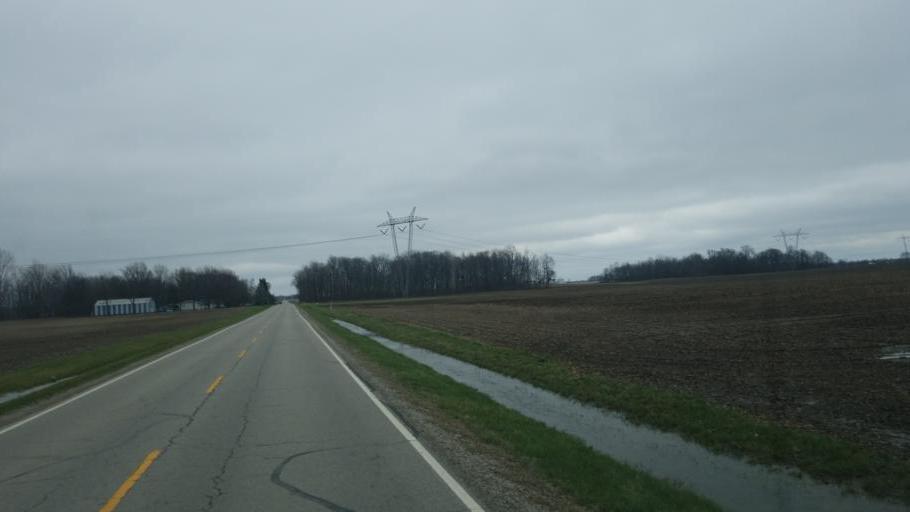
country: US
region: Ohio
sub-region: Crawford County
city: Bucyrus
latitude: 40.8193
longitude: -83.0437
